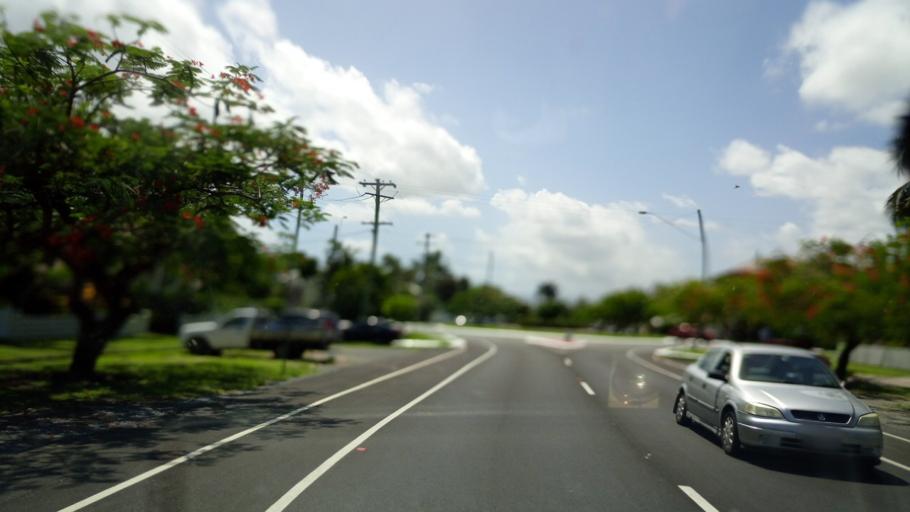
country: AU
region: Queensland
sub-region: Cairns
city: Cairns
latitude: -16.9174
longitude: 145.7627
